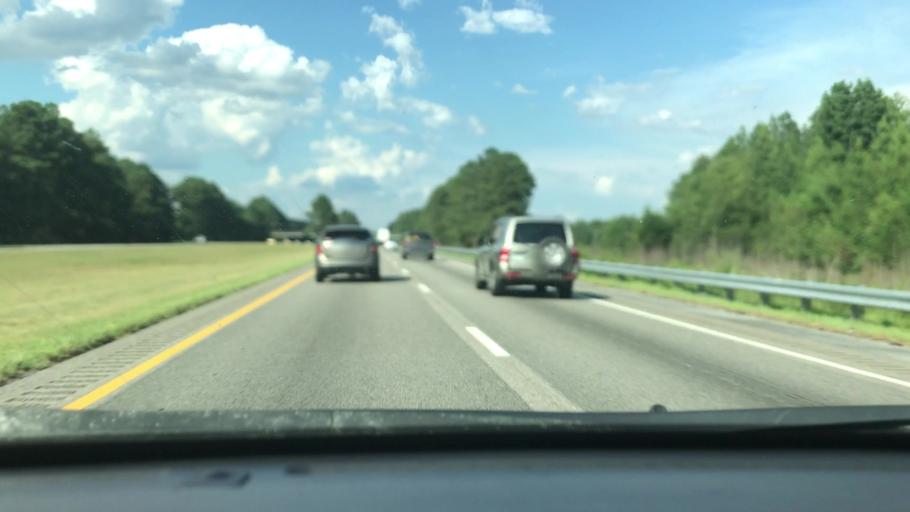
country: US
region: South Carolina
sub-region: Florence County
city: Timmonsville
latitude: 33.9829
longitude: -80.0301
